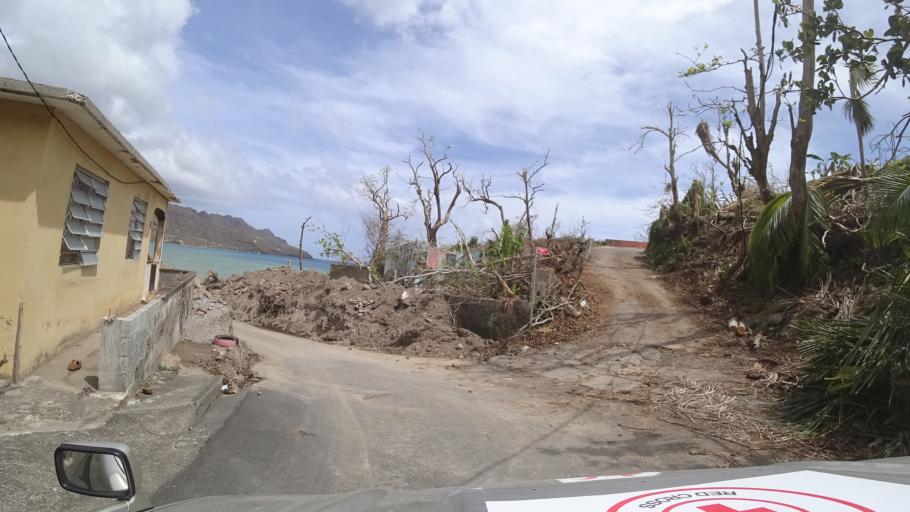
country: DM
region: Saint Patrick
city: Berekua
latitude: 15.2396
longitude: -61.3130
